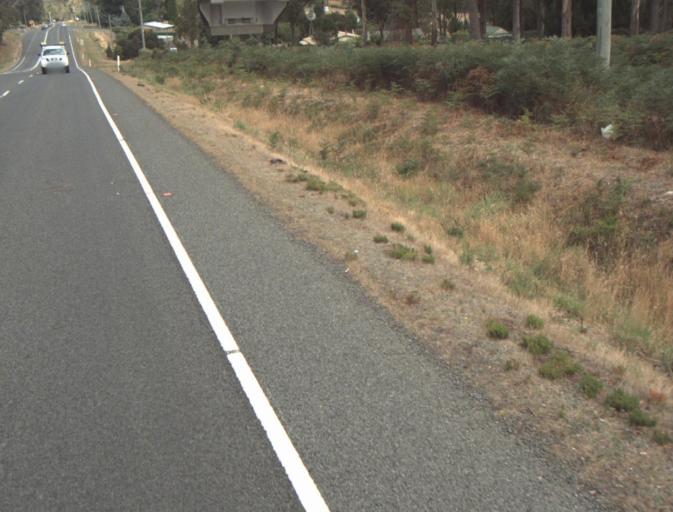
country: AU
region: Tasmania
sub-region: Launceston
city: Mayfield
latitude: -41.2804
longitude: 147.0384
